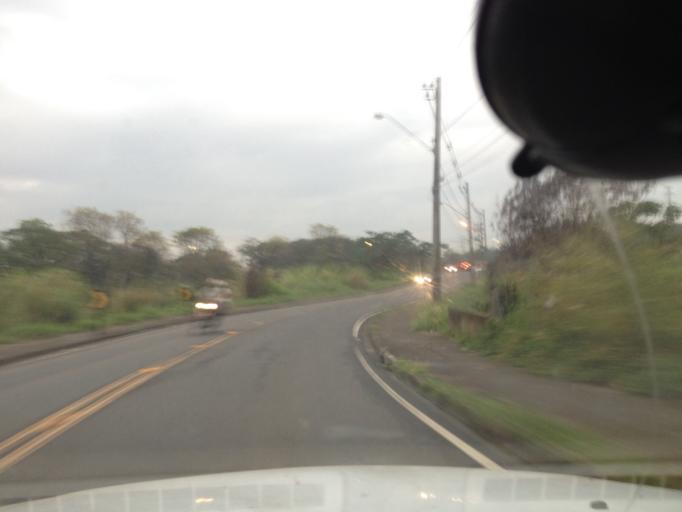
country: BR
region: Sao Paulo
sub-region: Salto
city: Salto
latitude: -23.1987
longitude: -47.2671
